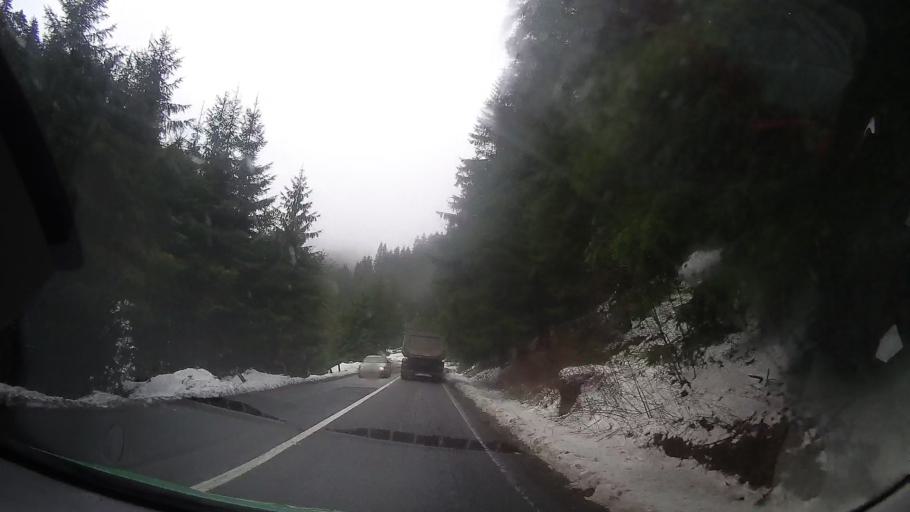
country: RO
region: Neamt
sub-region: Comuna Bicaz Chei
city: Bicaz Chei
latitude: 46.7818
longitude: 25.7495
